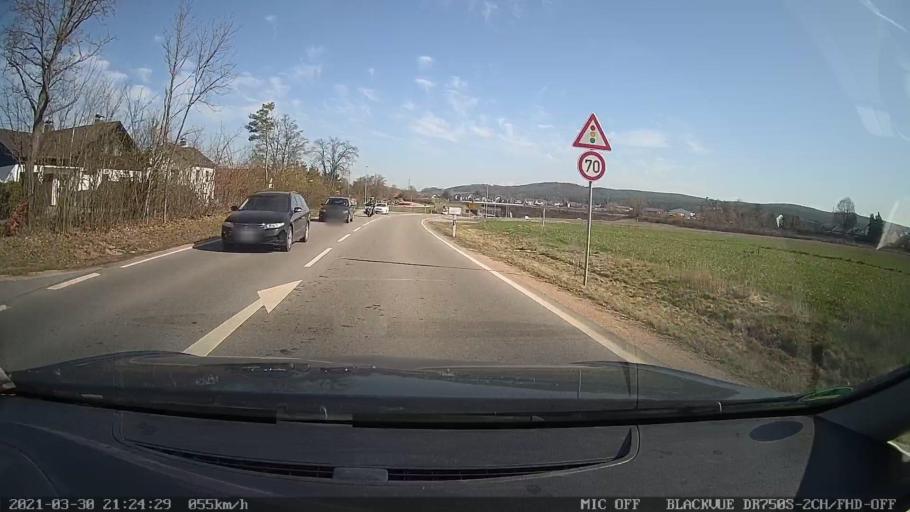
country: DE
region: Bavaria
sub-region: Upper Palatinate
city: Zeitlarn
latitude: 49.0872
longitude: 12.1196
